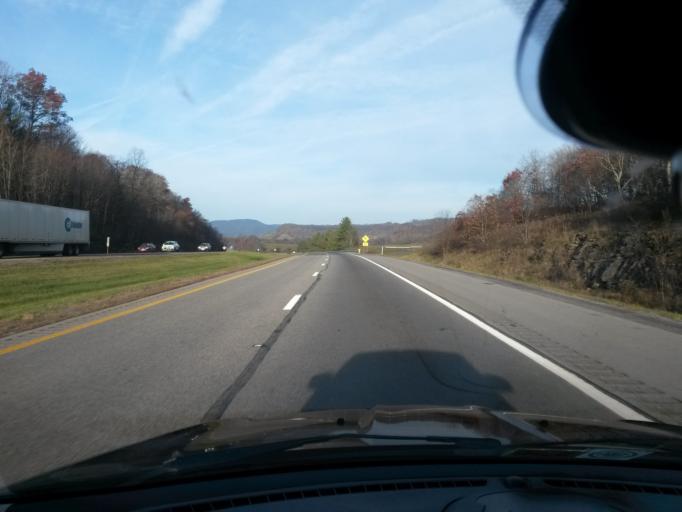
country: US
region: West Virginia
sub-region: Greenbrier County
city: Lewisburg
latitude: 37.9036
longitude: -80.5966
